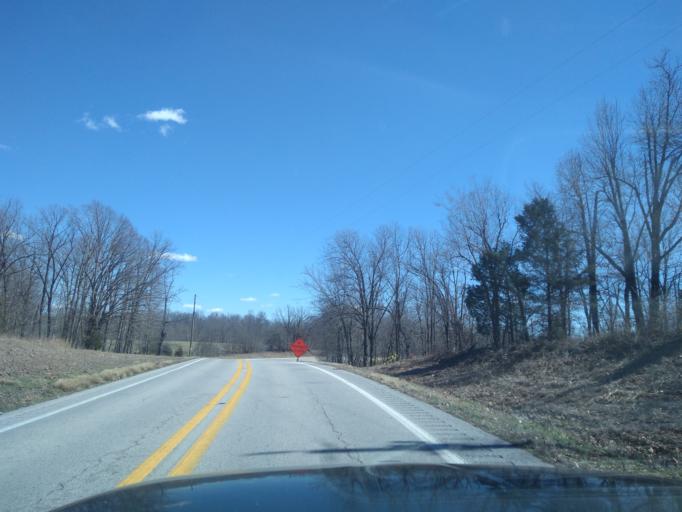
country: US
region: Arkansas
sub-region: Washington County
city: Farmington
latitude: 36.0883
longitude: -94.3291
